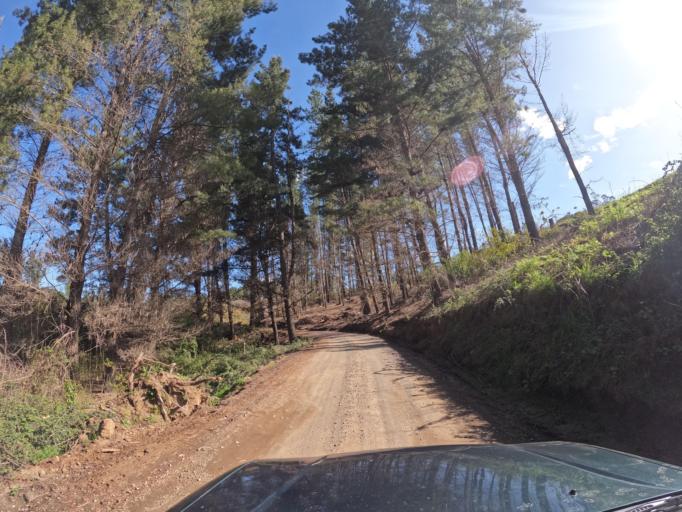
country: CL
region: Biobio
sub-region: Provincia de Biobio
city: La Laja
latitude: -37.0788
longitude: -72.8361
